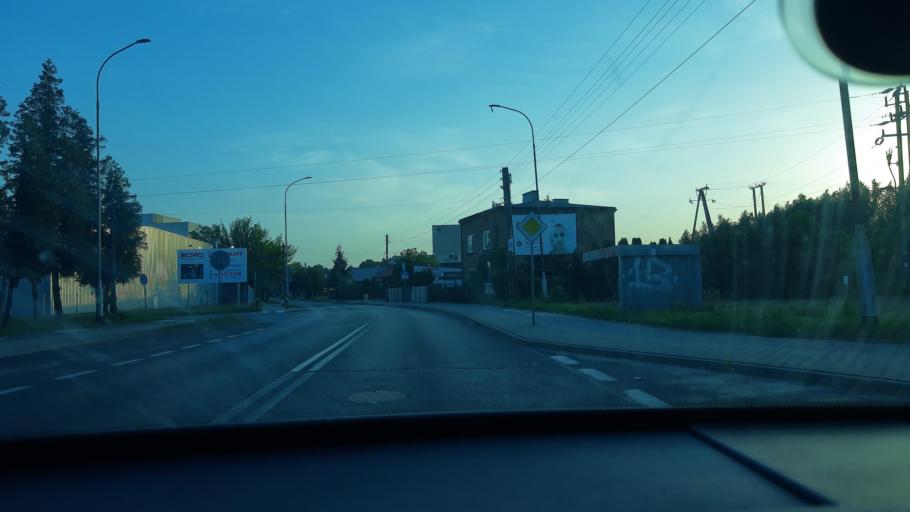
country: PL
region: Lodz Voivodeship
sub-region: Powiat zdunskowolski
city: Zdunska Wola
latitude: 51.6107
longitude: 18.9555
